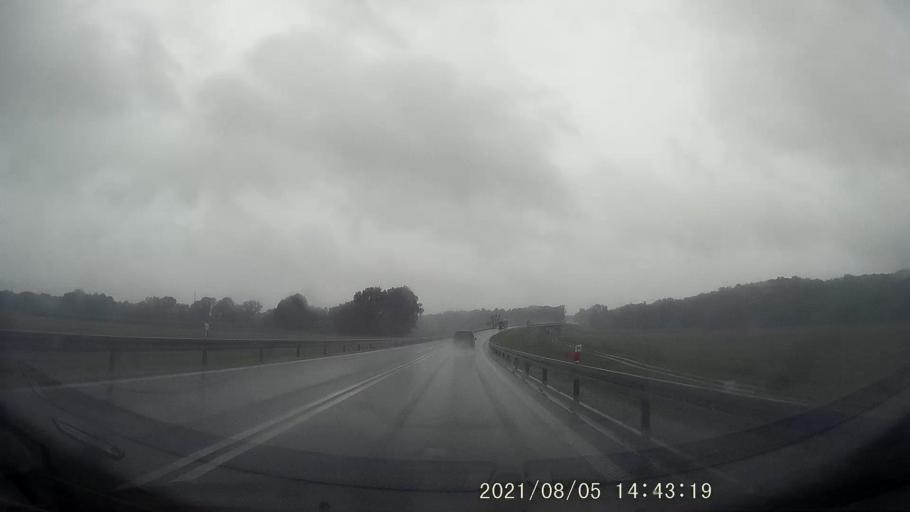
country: PL
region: Opole Voivodeship
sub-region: Powiat nyski
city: Nysa
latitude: 50.4818
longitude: 17.3911
